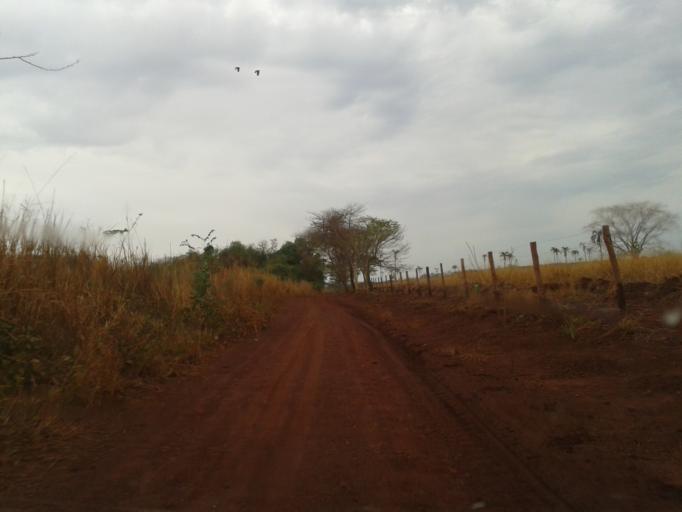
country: BR
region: Minas Gerais
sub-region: Capinopolis
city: Capinopolis
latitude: -18.8740
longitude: -49.7913
